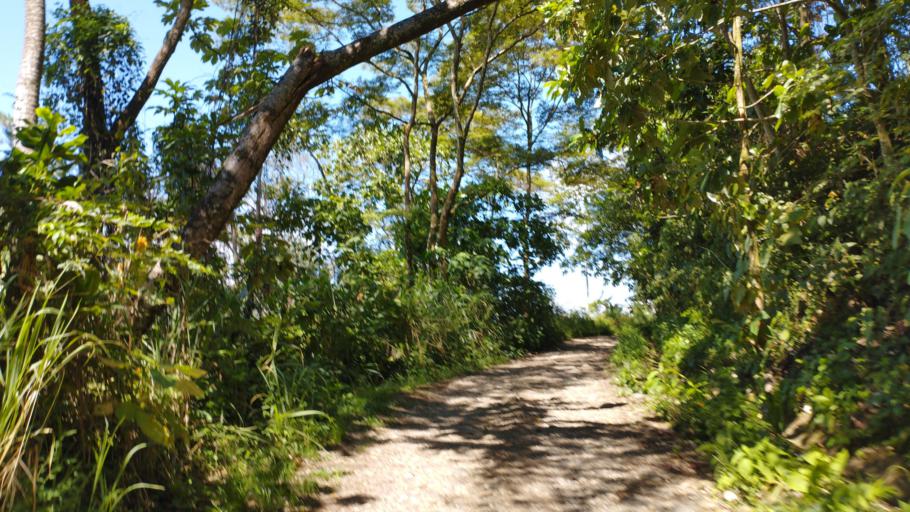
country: CO
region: Boyaca
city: San Luis de Gaceno
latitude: 4.7912
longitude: -73.1060
